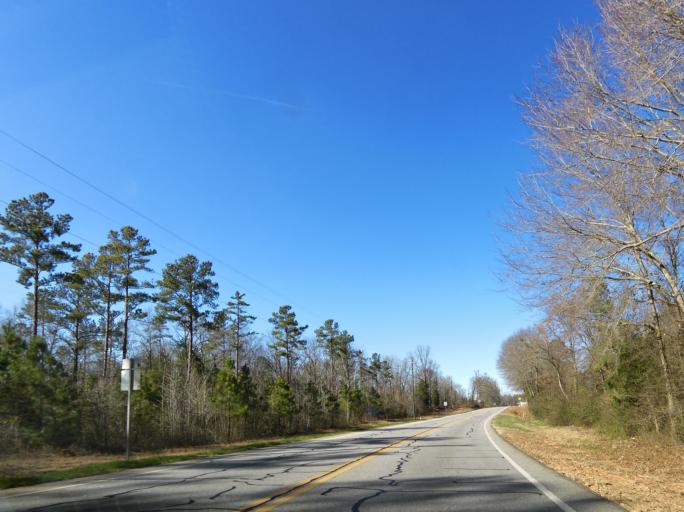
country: US
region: Georgia
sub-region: Lamar County
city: Barnesville
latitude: 32.9086
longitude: -84.1219
